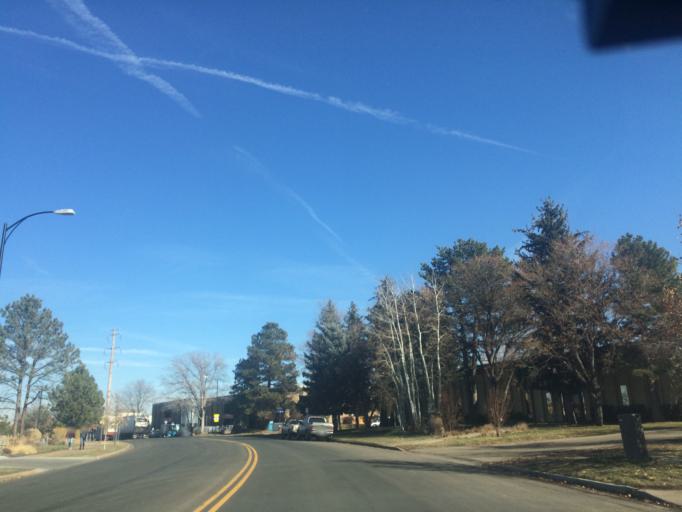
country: US
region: Colorado
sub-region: Boulder County
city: Boulder
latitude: 40.0197
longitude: -105.2198
